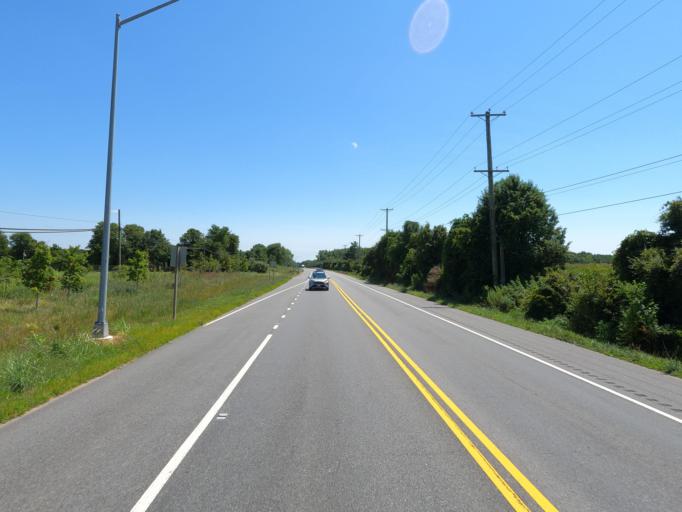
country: US
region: Maryland
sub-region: Cecil County
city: Elkton
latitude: 39.5865
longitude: -75.8229
